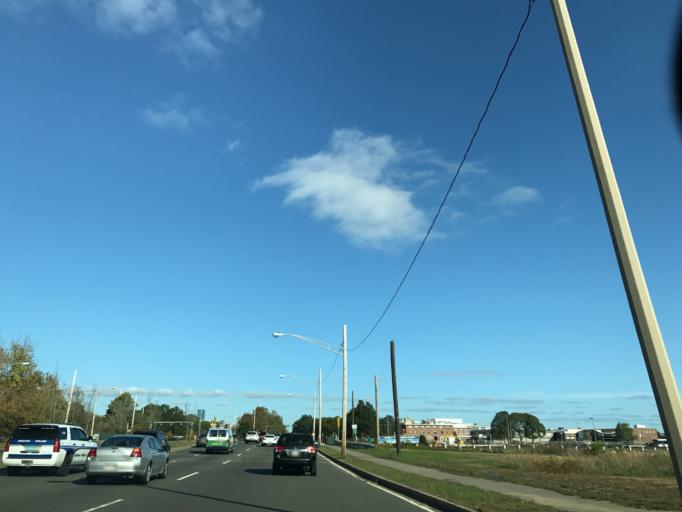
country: US
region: Massachusetts
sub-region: Suffolk County
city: South Boston
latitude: 42.3120
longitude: -71.0458
